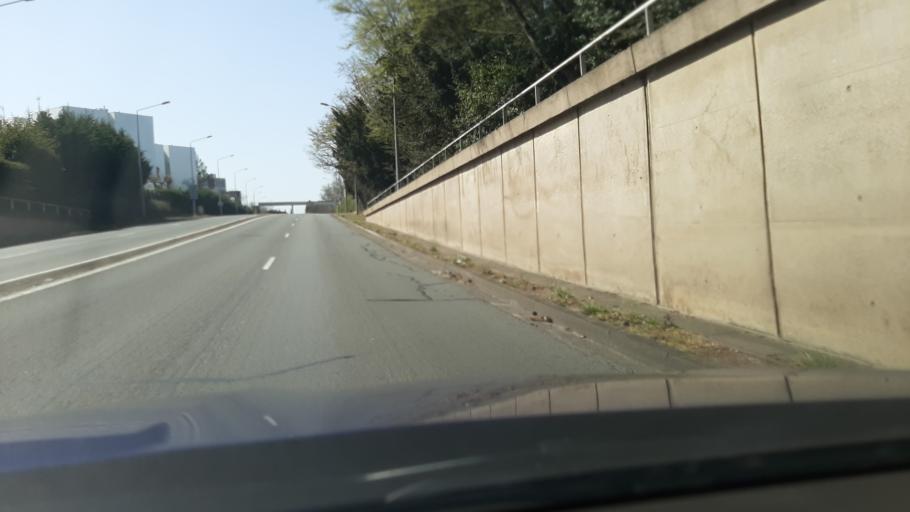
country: FR
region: Pays de la Loire
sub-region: Departement de Maine-et-Loire
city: Angers
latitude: 47.4591
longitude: -0.5224
